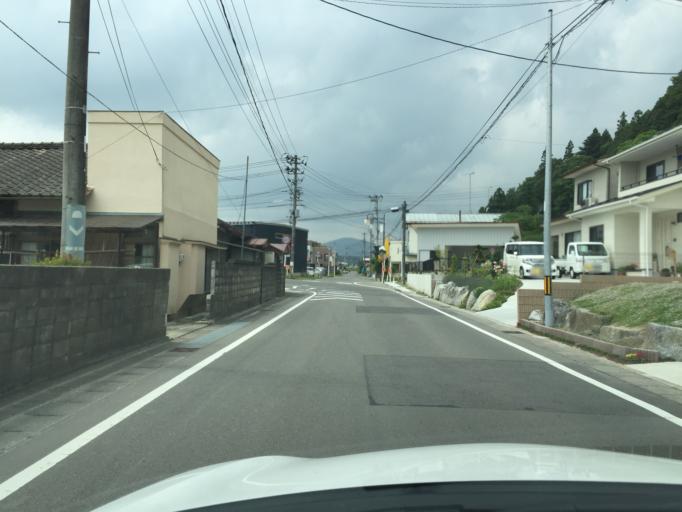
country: JP
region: Fukushima
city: Funehikimachi-funehiki
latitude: 37.2737
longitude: 140.6398
